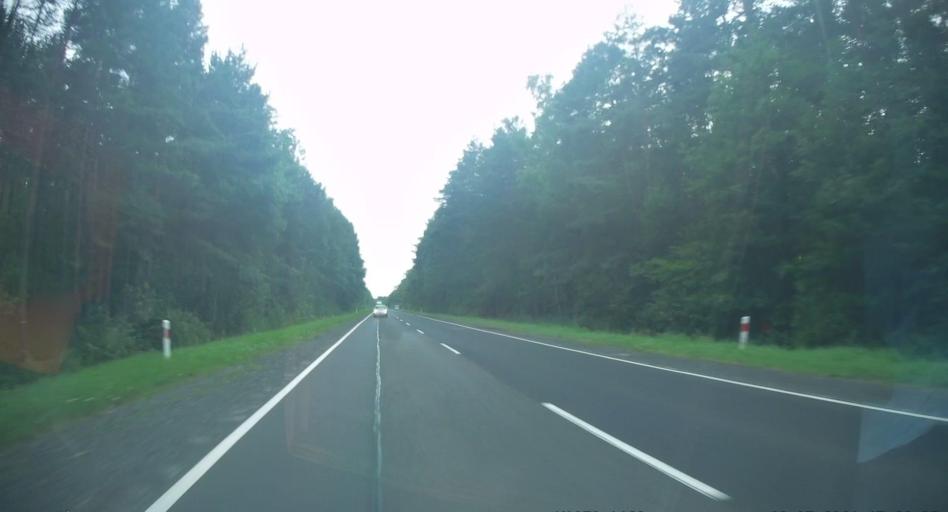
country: PL
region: Lodz Voivodeship
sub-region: Powiat radomszczanski
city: Radomsko
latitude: 51.0312
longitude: 19.4352
